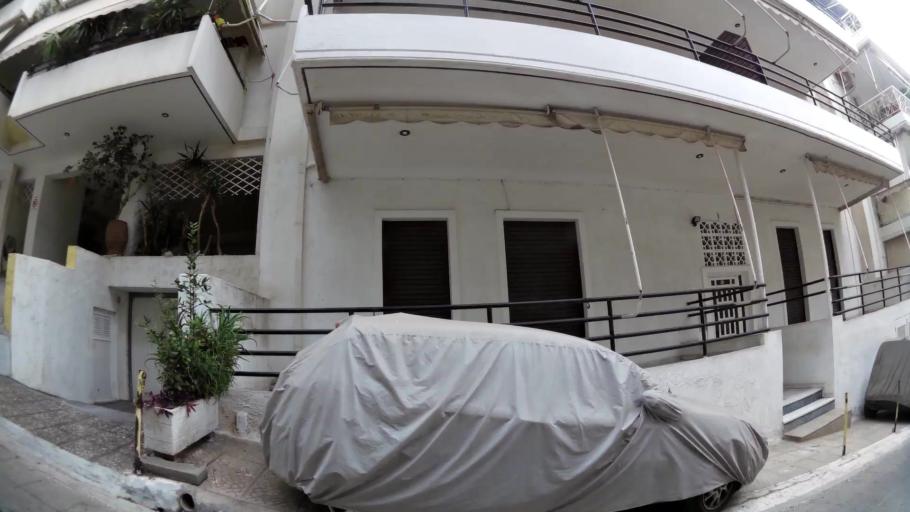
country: GR
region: Attica
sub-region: Nomos Attikis
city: Piraeus
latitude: 37.9290
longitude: 23.6430
